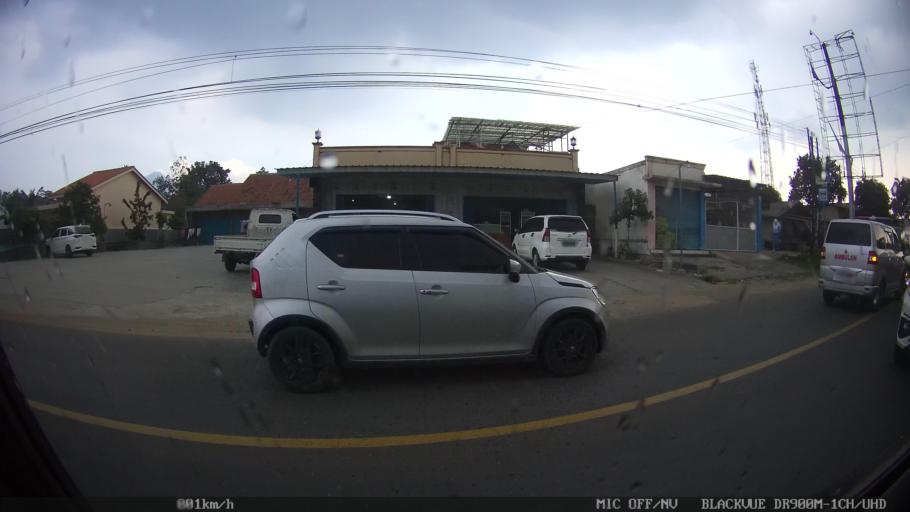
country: ID
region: Lampung
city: Gedongtataan
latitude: -5.3799
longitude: 105.1092
